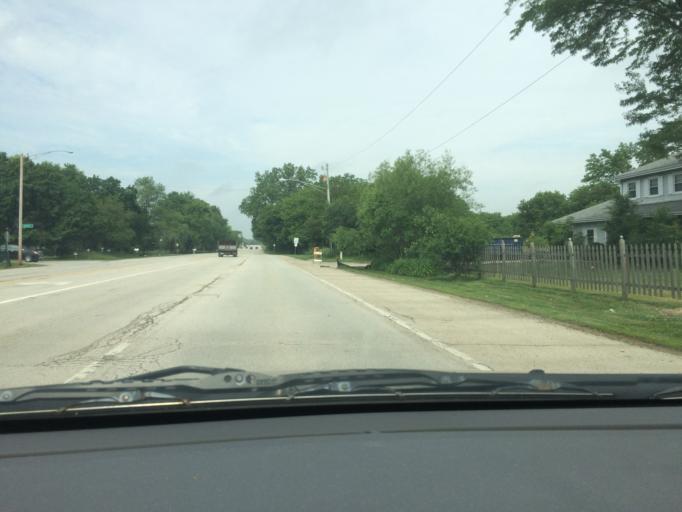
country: US
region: Illinois
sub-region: Cook County
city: Bartlett
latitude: 41.9440
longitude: -88.1834
